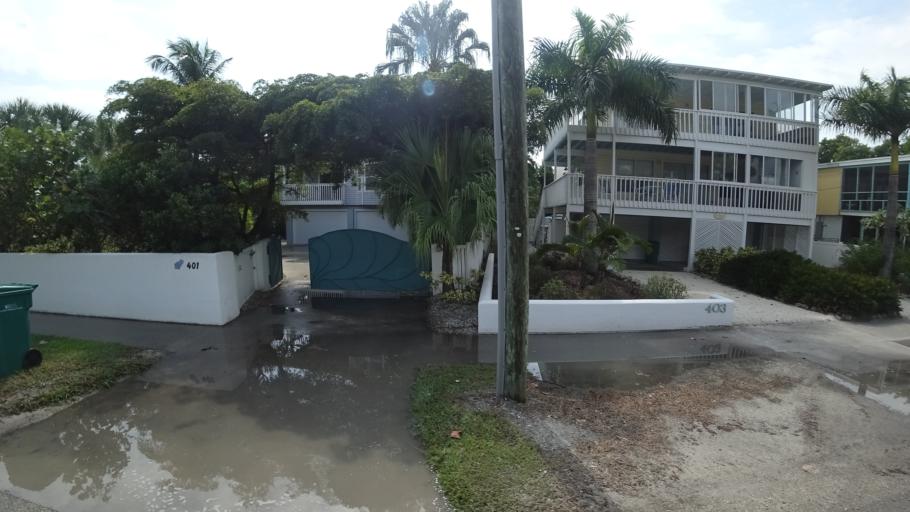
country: US
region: Florida
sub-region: Manatee County
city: Anna Maria
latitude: 27.5348
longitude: -82.7362
